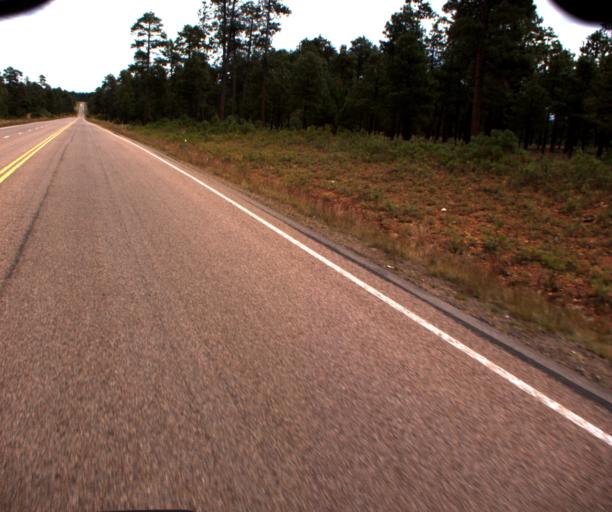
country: US
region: Arizona
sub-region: Navajo County
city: Heber-Overgaard
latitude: 34.3348
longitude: -110.7481
